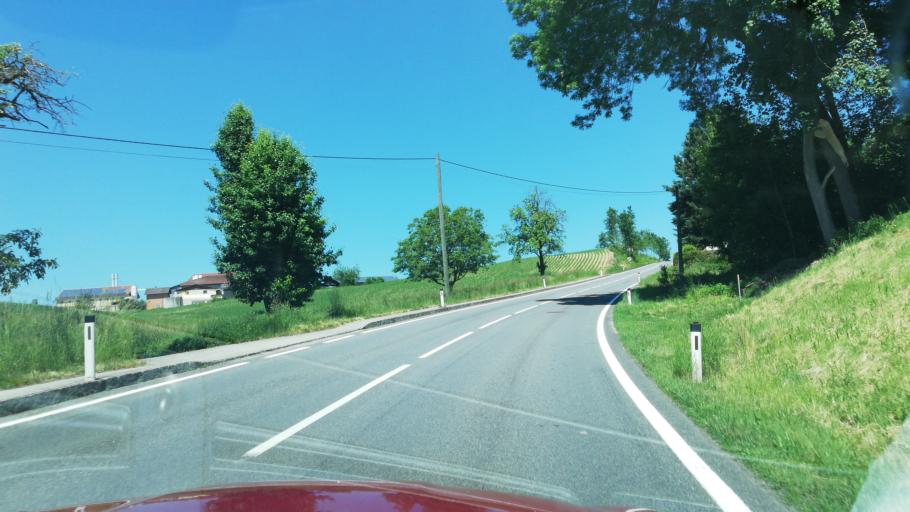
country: AT
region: Upper Austria
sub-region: Politischer Bezirk Vocklabruck
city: Niederthalheim
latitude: 48.0795
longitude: 13.7614
